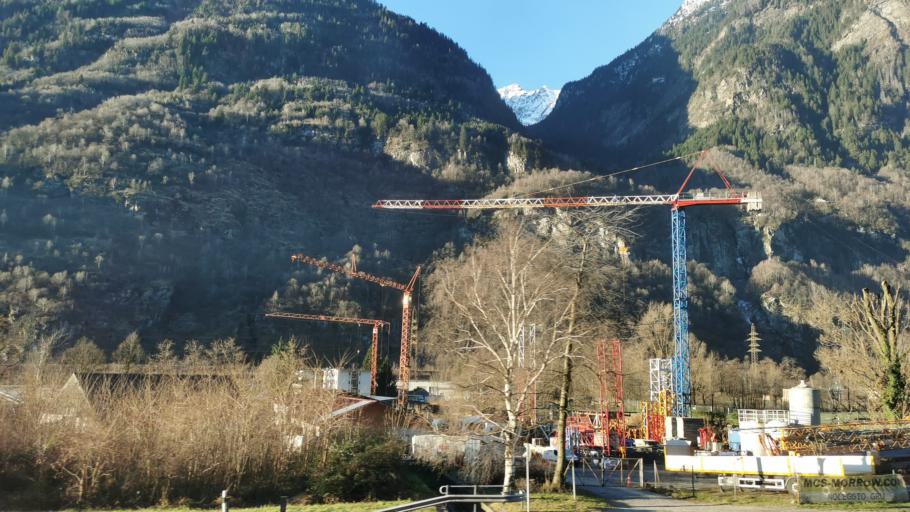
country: CH
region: Ticino
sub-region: Leventina District
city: Bodio
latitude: 46.3927
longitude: 8.8904
